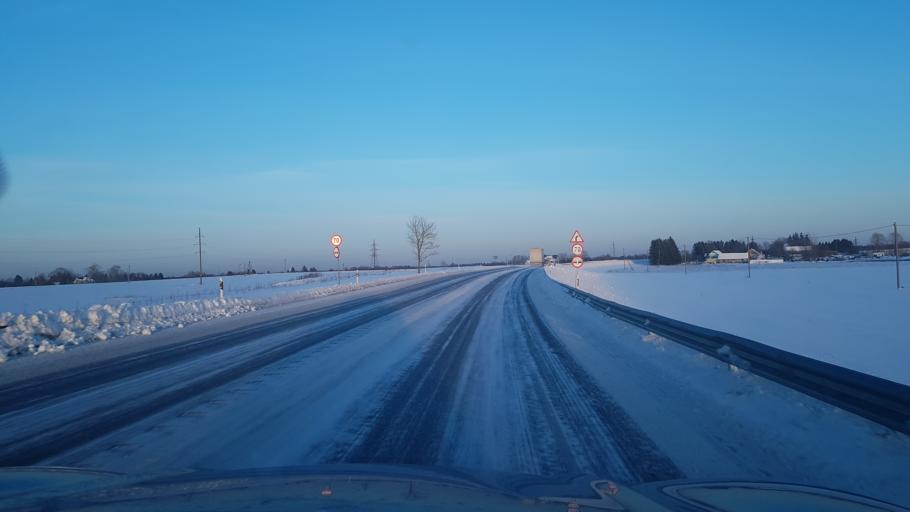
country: EE
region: Ida-Virumaa
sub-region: Narva-Joesuu linn
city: Narva-Joesuu
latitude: 59.4053
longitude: 28.0214
